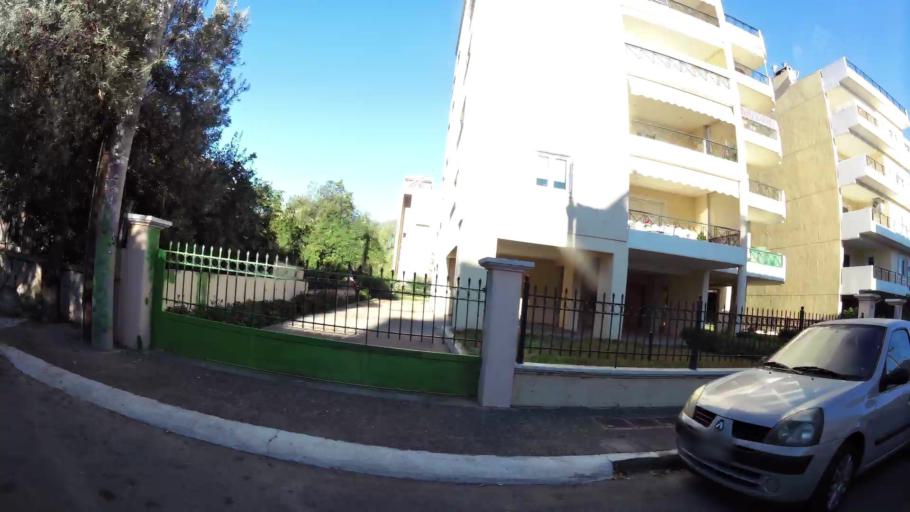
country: GR
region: Attica
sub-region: Nomarchia Athinas
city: Neo Psychiko
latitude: 38.0110
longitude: 23.7925
